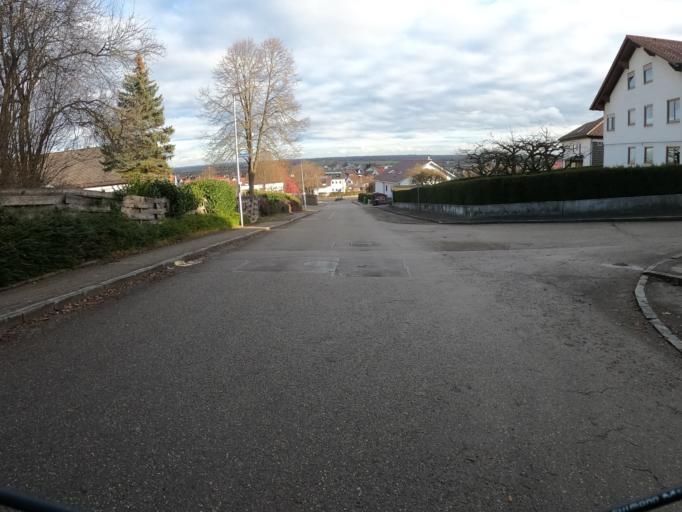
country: DE
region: Bavaria
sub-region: Swabia
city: Nersingen
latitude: 48.4577
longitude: 10.1001
